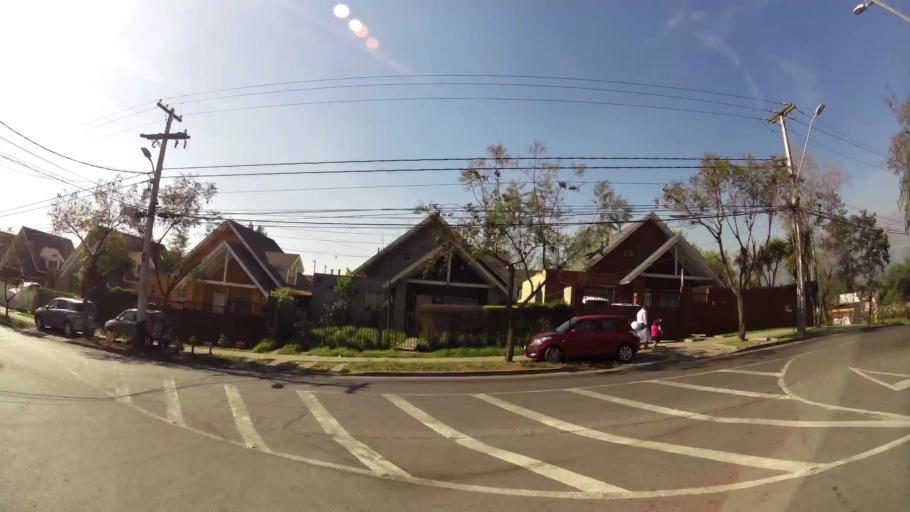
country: CL
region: Santiago Metropolitan
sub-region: Provincia de Santiago
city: Villa Presidente Frei, Nunoa, Santiago, Chile
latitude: -33.4861
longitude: -70.5589
